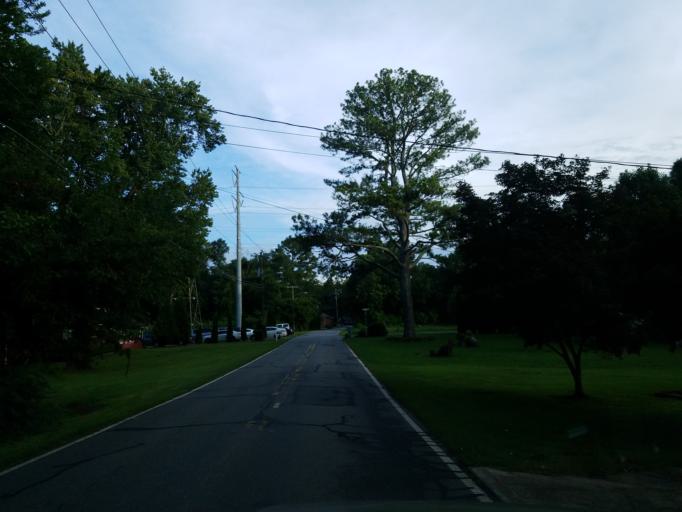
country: US
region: Georgia
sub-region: Bartow County
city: Cartersville
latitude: 34.1811
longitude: -84.7983
